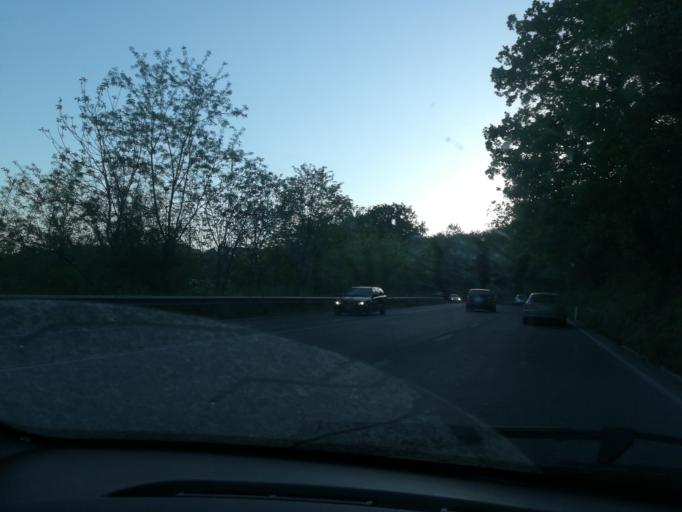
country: IT
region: The Marches
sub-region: Provincia di Macerata
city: Piediripa
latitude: 43.2856
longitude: 13.4763
